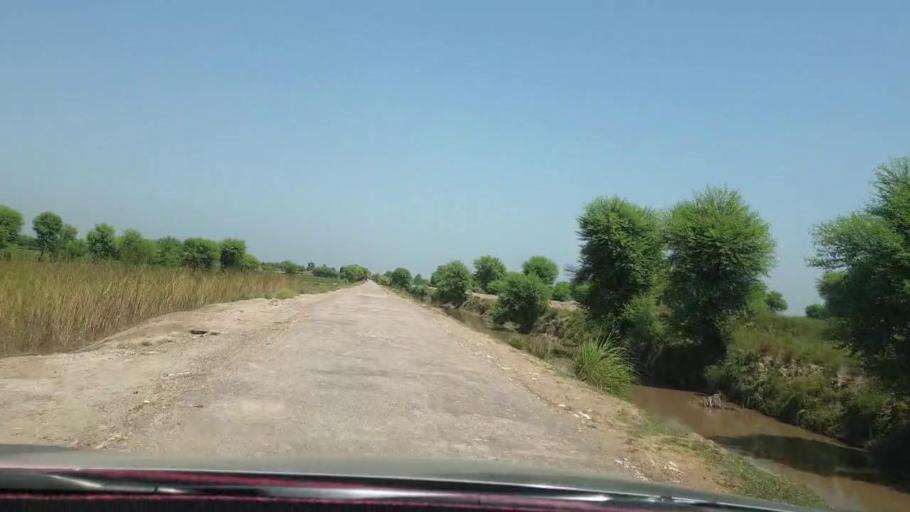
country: PK
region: Sindh
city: Warah
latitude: 27.5174
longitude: 67.8104
